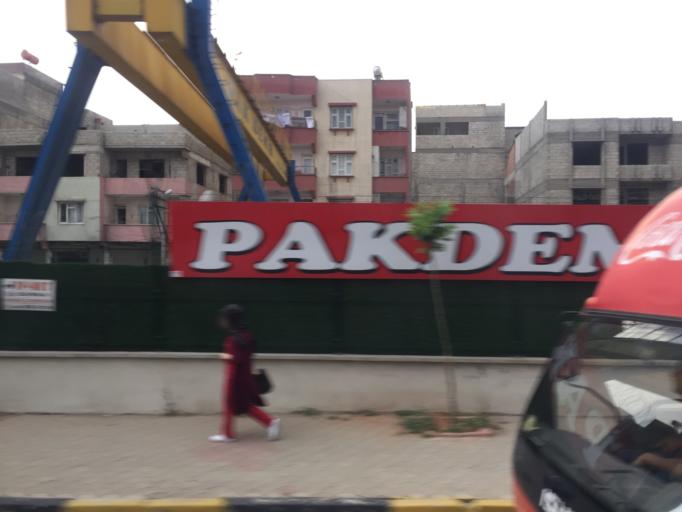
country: TR
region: Gaziantep
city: Gaziantep
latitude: 37.0640
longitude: 37.4151
